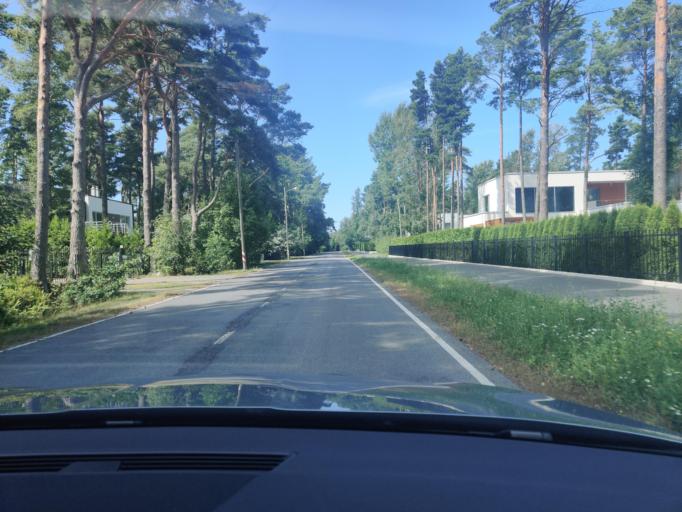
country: EE
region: Harju
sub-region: Harku vald
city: Tabasalu
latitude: 59.4571
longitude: 24.5760
